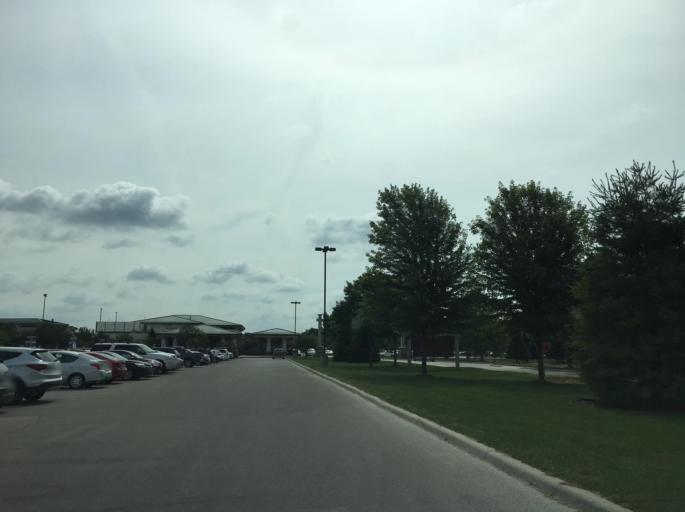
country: US
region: Michigan
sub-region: Grand Traverse County
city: Traverse City
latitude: 44.7367
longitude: -85.5823
